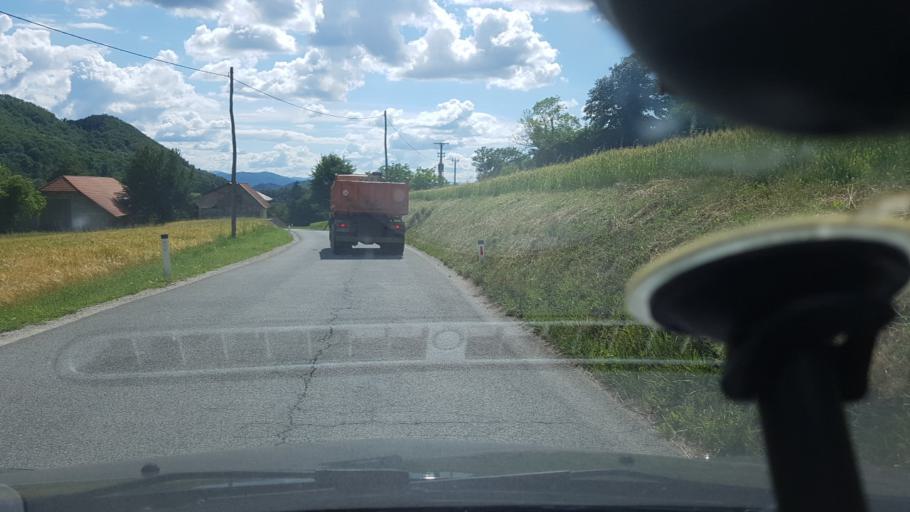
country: SI
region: Rogatec
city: Rogatec
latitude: 46.2546
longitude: 15.7497
